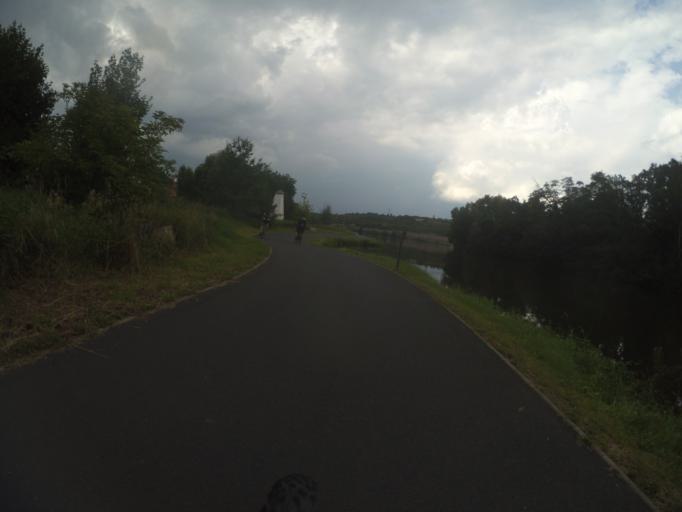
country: CZ
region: Central Bohemia
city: Dolni Berkovice
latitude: 50.3925
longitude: 14.4567
